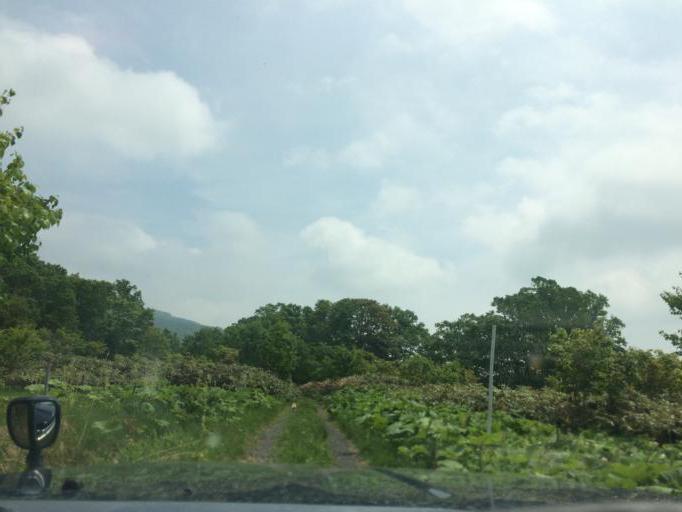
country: JP
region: Hokkaido
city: Niseko Town
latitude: 42.6796
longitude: 140.6116
